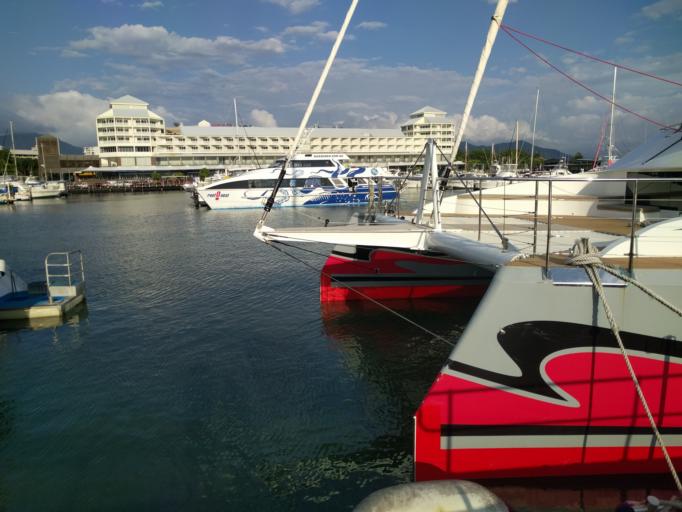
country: AU
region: Queensland
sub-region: Cairns
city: Cairns
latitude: -16.9205
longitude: 145.7825
